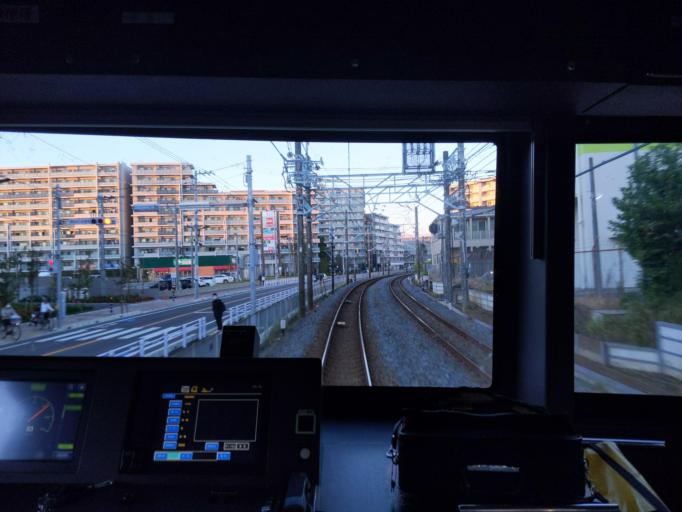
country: JP
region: Chiba
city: Funabashi
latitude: 35.7186
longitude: 139.9808
